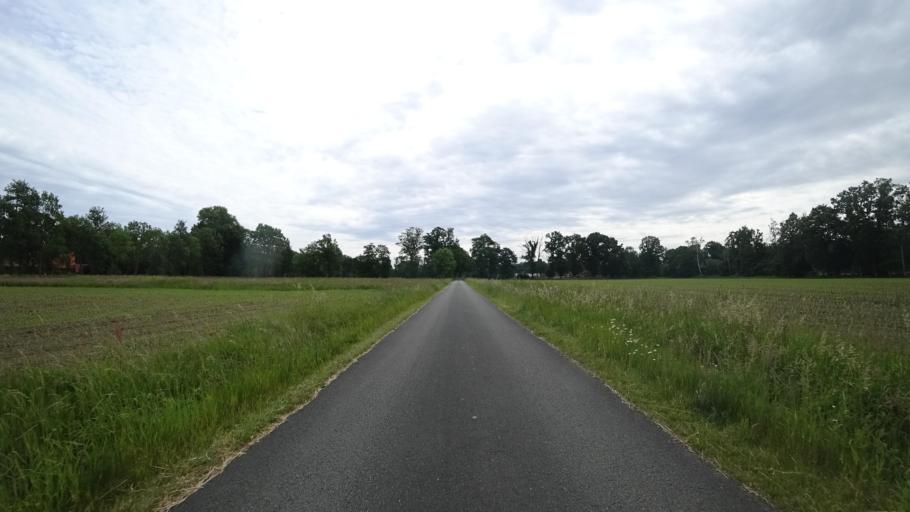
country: DE
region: North Rhine-Westphalia
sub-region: Regierungsbezirk Detmold
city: Guetersloh
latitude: 51.9156
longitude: 8.3331
